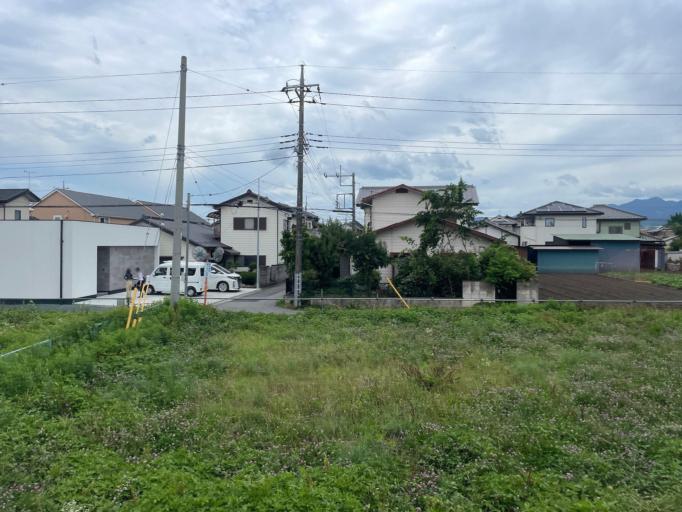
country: JP
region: Gunma
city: Kanekomachi
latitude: 36.4155
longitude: 139.0322
